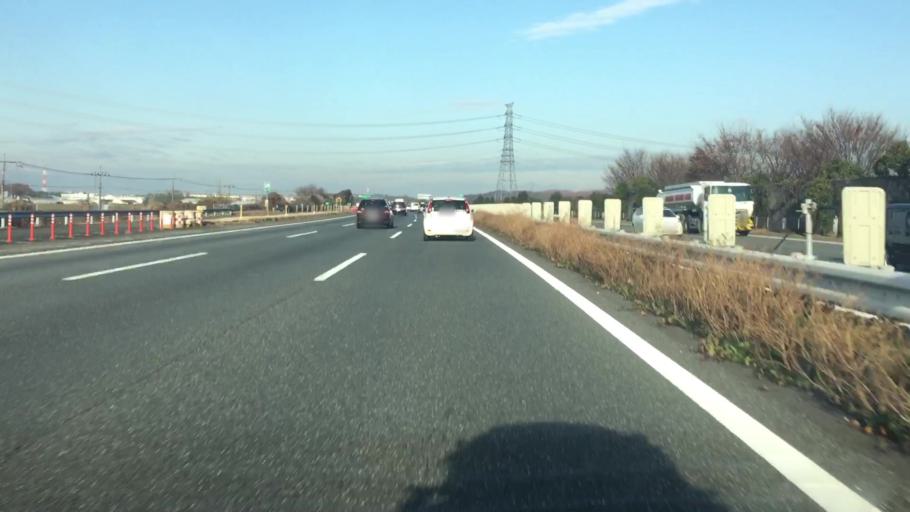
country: JP
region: Saitama
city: Honjo
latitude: 36.1996
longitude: 139.1830
